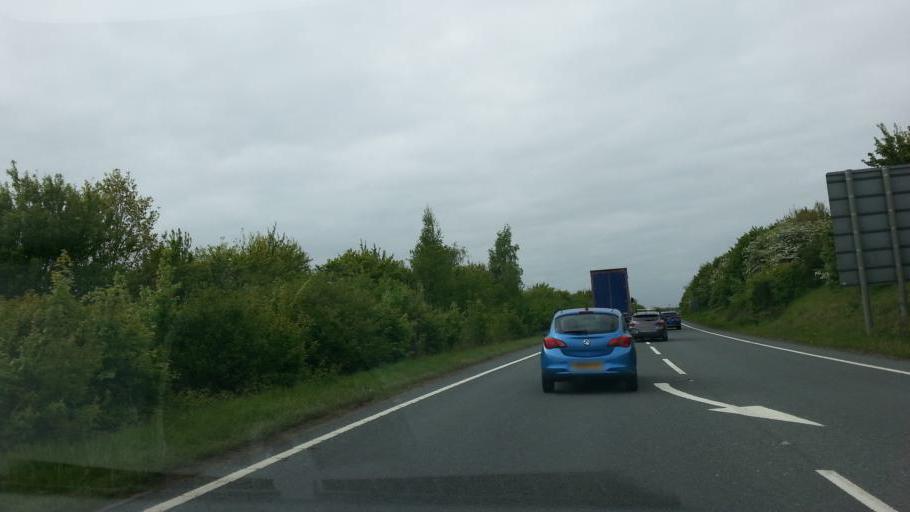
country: GB
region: England
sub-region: Lincolnshire
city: Sutton Bridge
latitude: 52.7777
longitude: 0.1114
